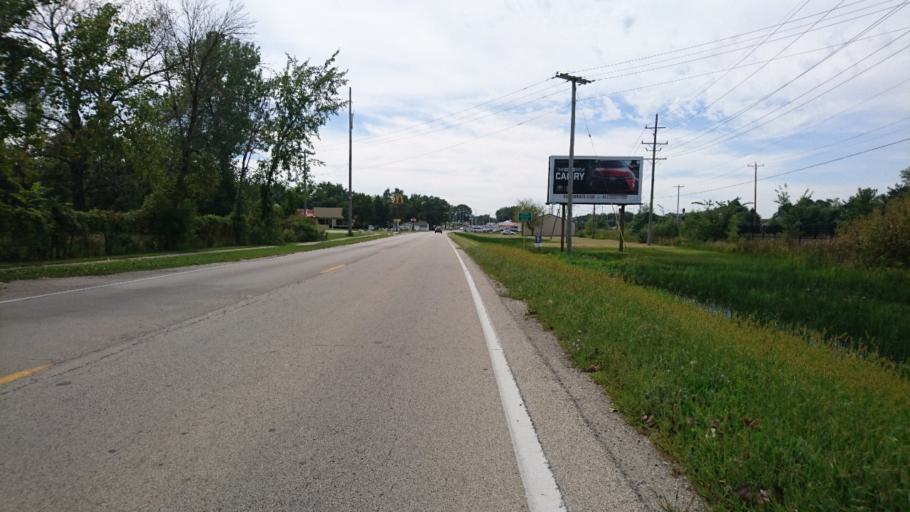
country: US
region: Illinois
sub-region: Will County
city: Braidwood
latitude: 41.2671
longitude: -88.2077
